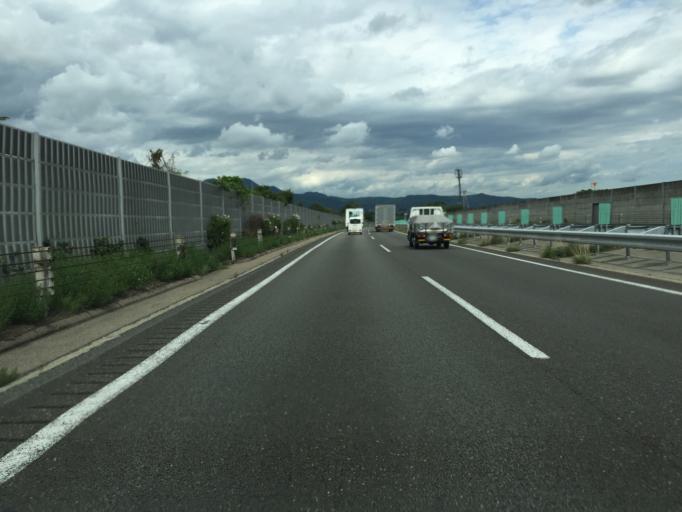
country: JP
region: Miyagi
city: Shiroishi
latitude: 37.9908
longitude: 140.6065
